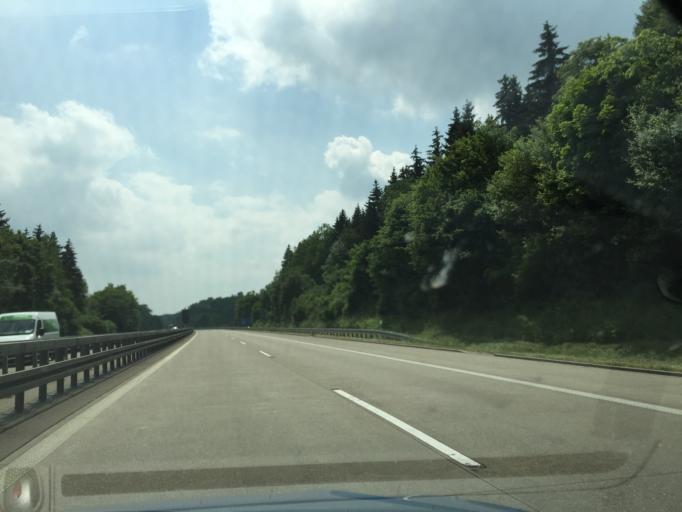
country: DE
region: Baden-Wuerttemberg
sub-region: Tuebingen Region
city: Nerenstetten
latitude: 48.5376
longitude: 10.0928
